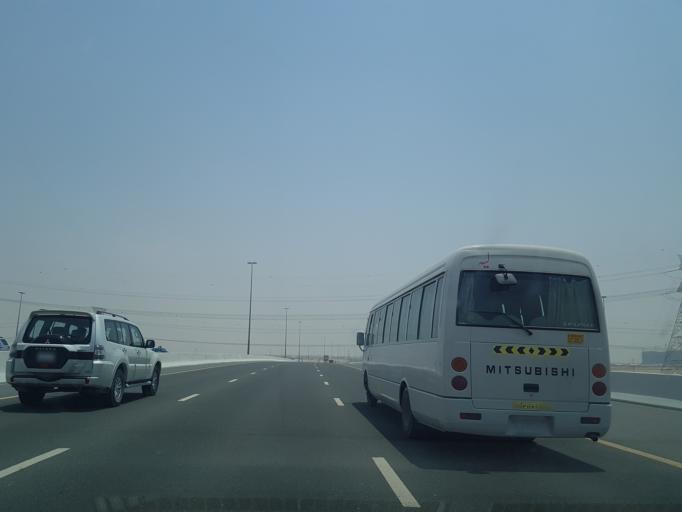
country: AE
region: Dubai
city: Dubai
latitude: 25.0228
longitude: 55.2800
